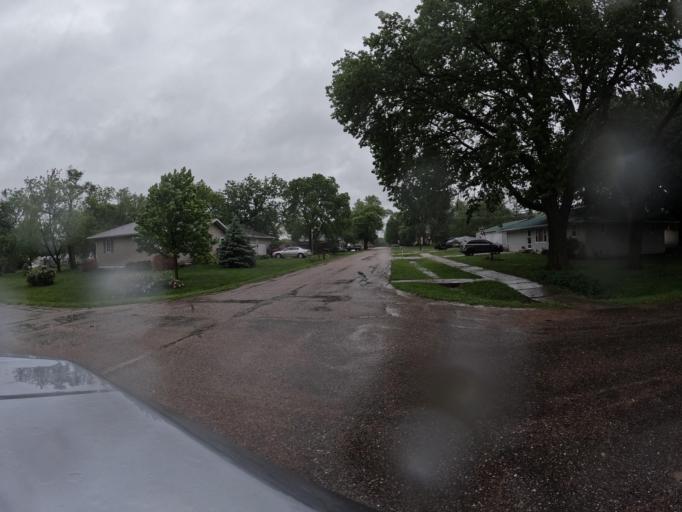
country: US
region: Nebraska
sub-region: Gage County
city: Wymore
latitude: 40.1204
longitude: -96.6753
